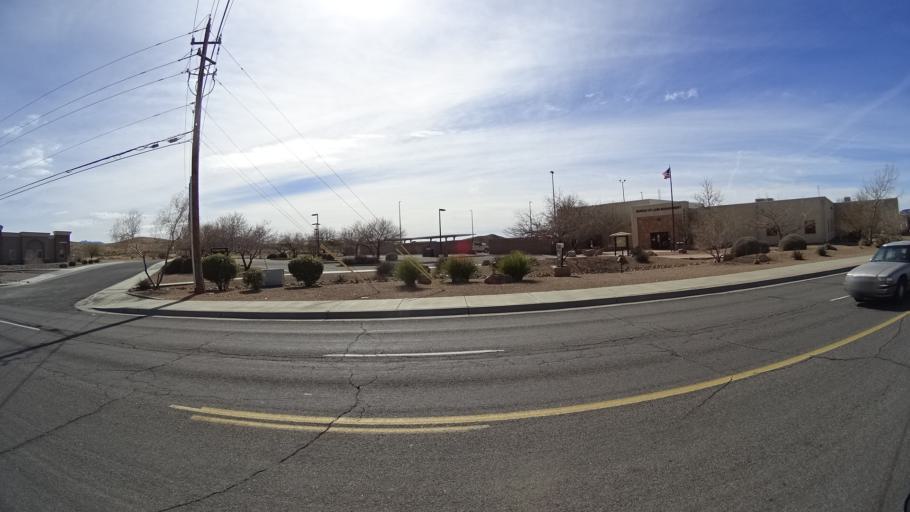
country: US
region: Arizona
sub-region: Mohave County
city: Kingman
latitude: 35.1901
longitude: -114.0134
